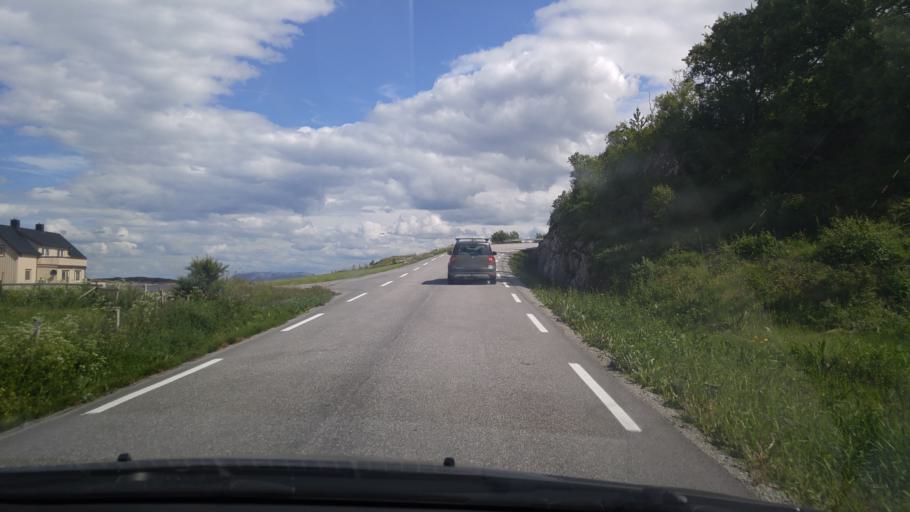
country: NO
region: Nord-Trondelag
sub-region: Vikna
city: Rorvik
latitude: 64.9199
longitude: 11.2316
